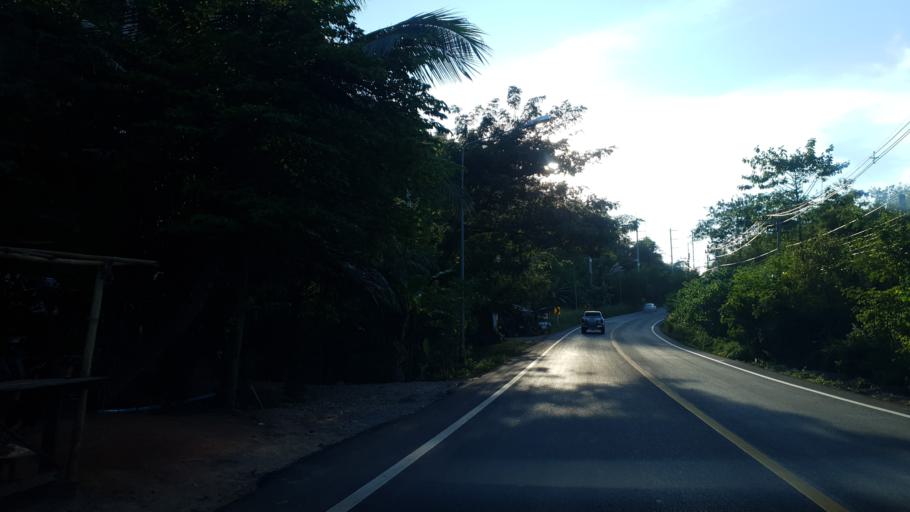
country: TH
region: Loei
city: Dan Sai
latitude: 17.2312
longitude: 101.0508
